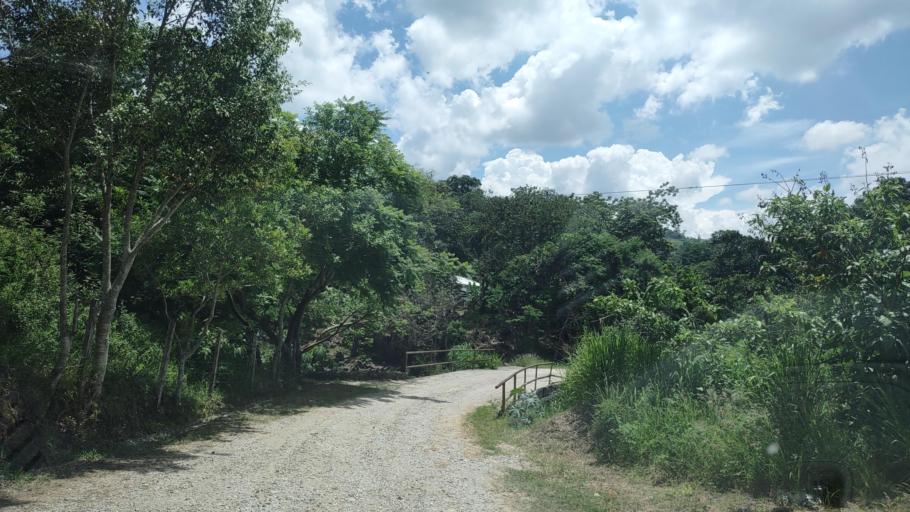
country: MX
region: Veracruz
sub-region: Emiliano Zapata
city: Dos Rios
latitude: 19.4968
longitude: -96.8112
